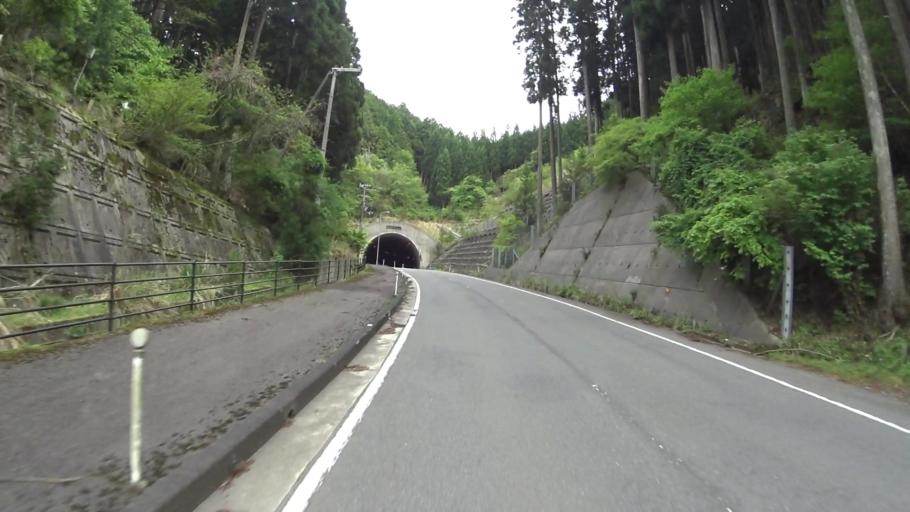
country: JP
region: Kyoto
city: Kameoka
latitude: 35.1295
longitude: 135.6207
